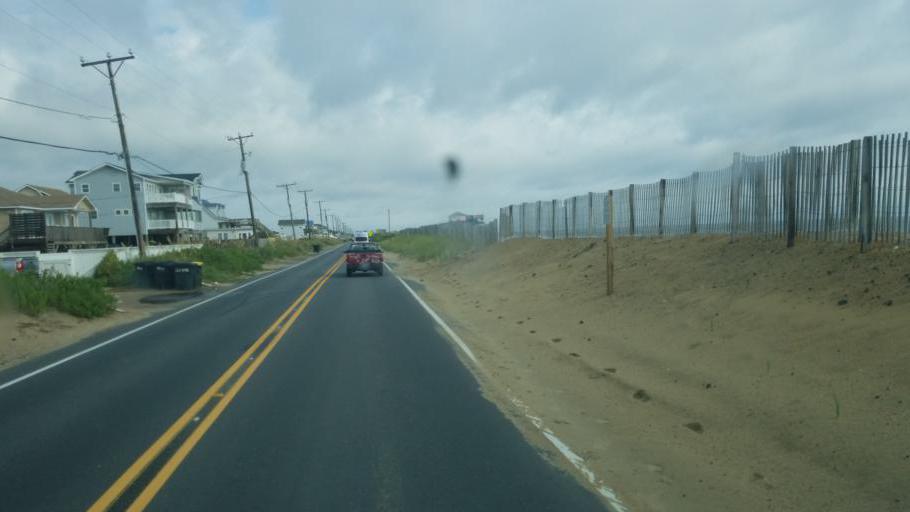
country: US
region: North Carolina
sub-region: Dare County
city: Kitty Hawk
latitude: 36.0683
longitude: -75.6913
